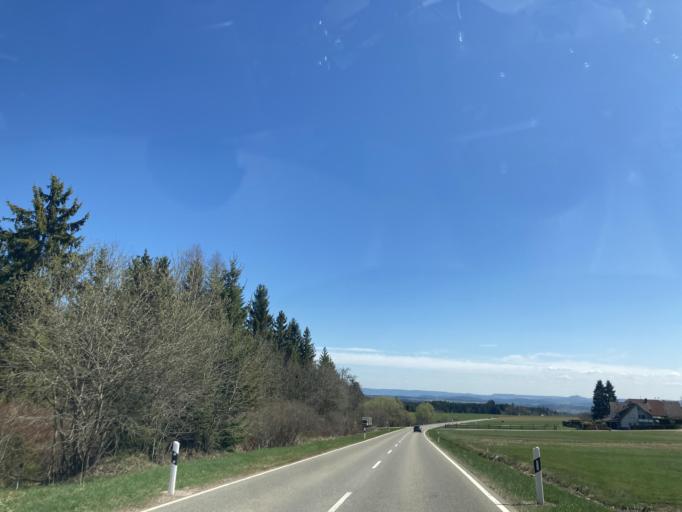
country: DE
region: Baden-Wuerttemberg
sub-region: Freiburg Region
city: Unterkirnach
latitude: 48.0268
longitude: 8.3684
